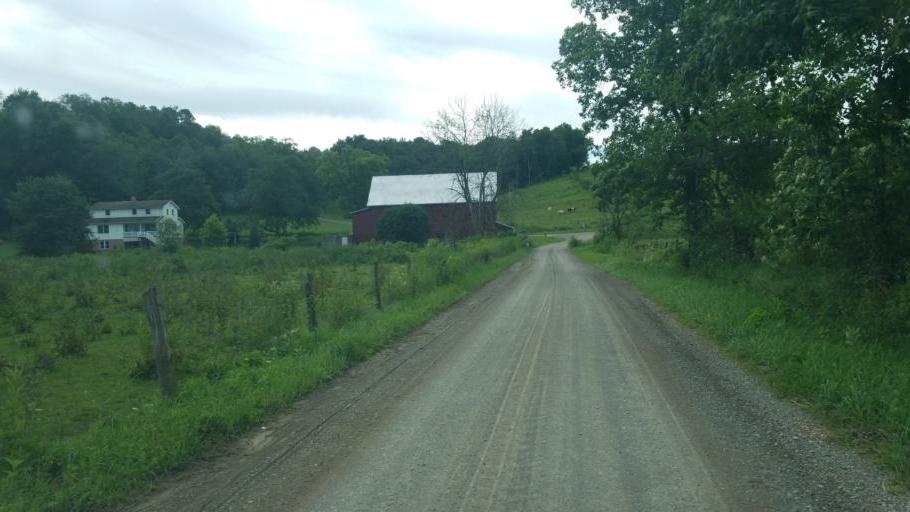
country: US
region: Ohio
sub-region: Holmes County
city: Millersburg
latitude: 40.4906
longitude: -81.8475
